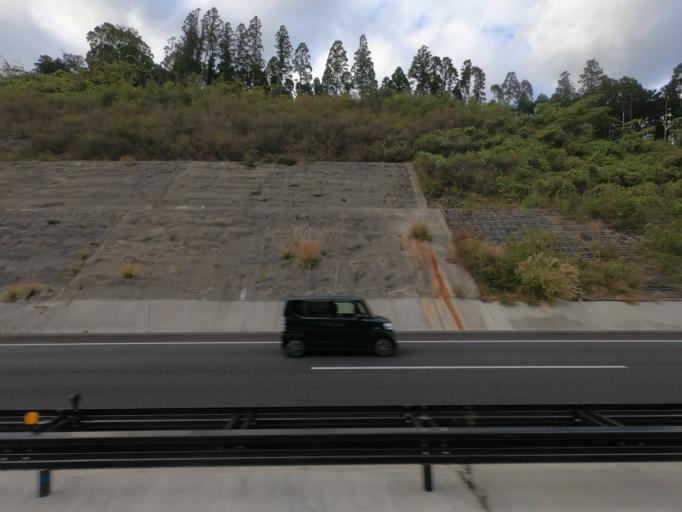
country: JP
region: Kumamoto
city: Minamata
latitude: 32.2396
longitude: 130.4618
